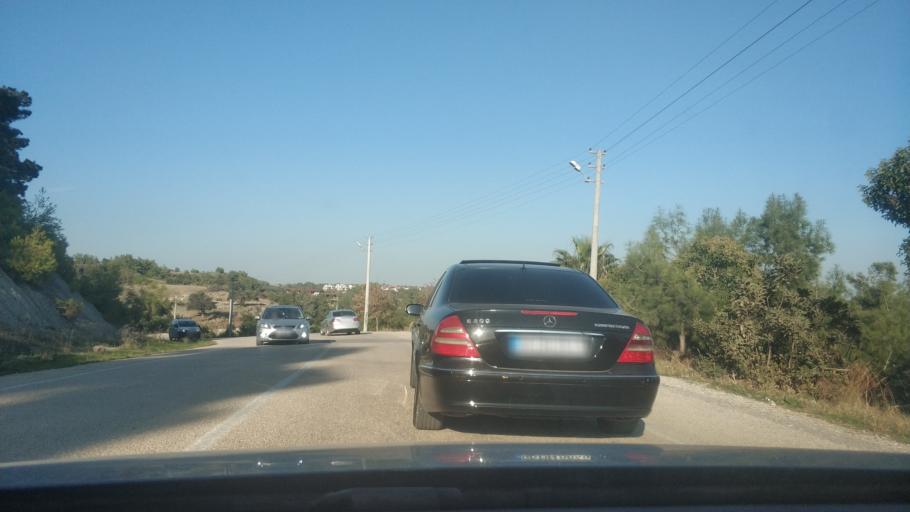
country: TR
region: Adana
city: Adana
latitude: 37.0999
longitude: 35.2906
